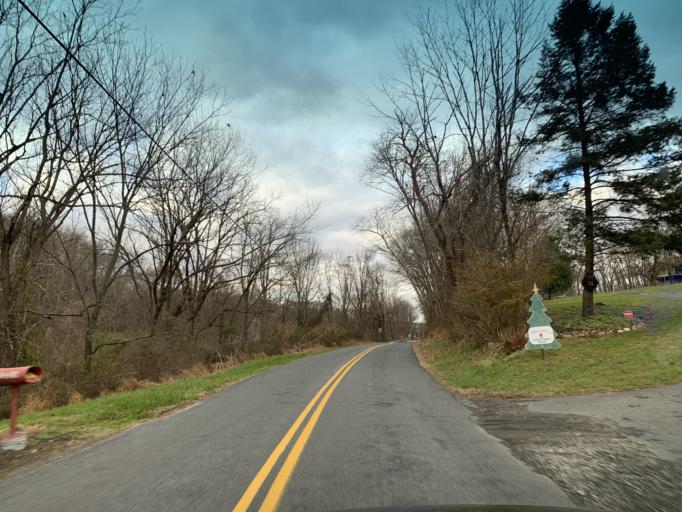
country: US
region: Maryland
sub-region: Harford County
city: Jarrettsville
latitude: 39.6502
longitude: -76.4367
